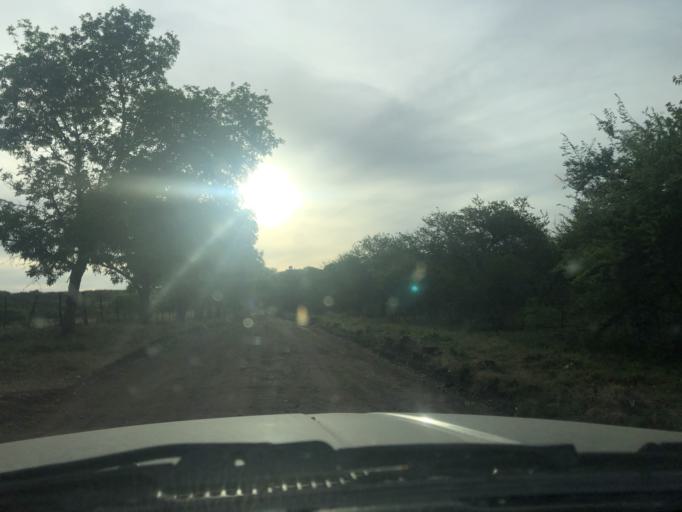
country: AR
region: Cordoba
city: La Granja
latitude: -31.0138
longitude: -64.2501
